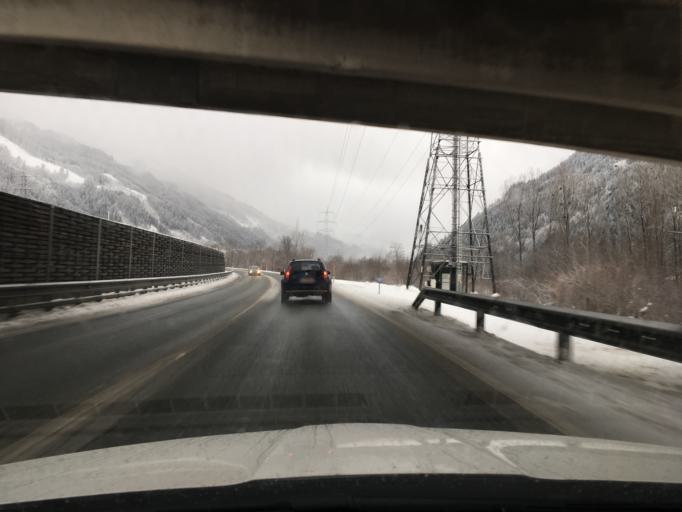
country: AT
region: Tyrol
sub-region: Politischer Bezirk Schwaz
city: Stumm
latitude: 47.2620
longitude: 11.8987
